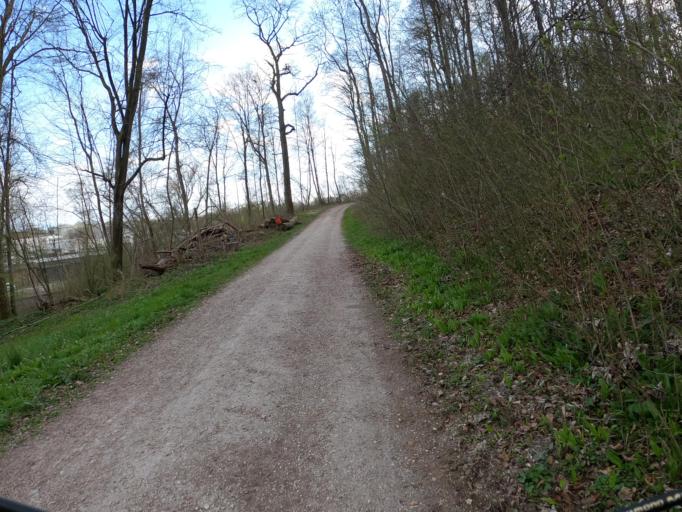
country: DE
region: Bavaria
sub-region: Swabia
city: Neu-Ulm
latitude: 48.4234
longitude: 10.0235
